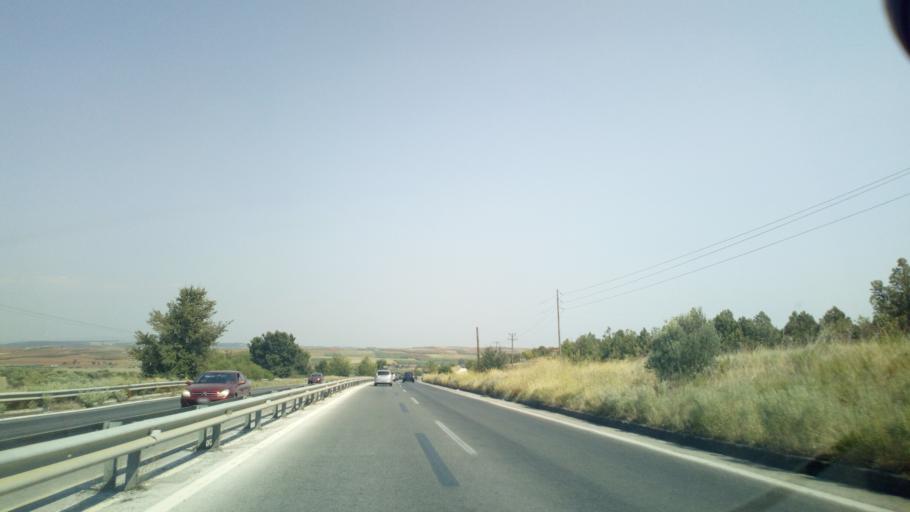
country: GR
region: Central Macedonia
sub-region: Nomos Chalkidikis
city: Nea Kallikrateia
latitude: 40.3125
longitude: 23.1071
